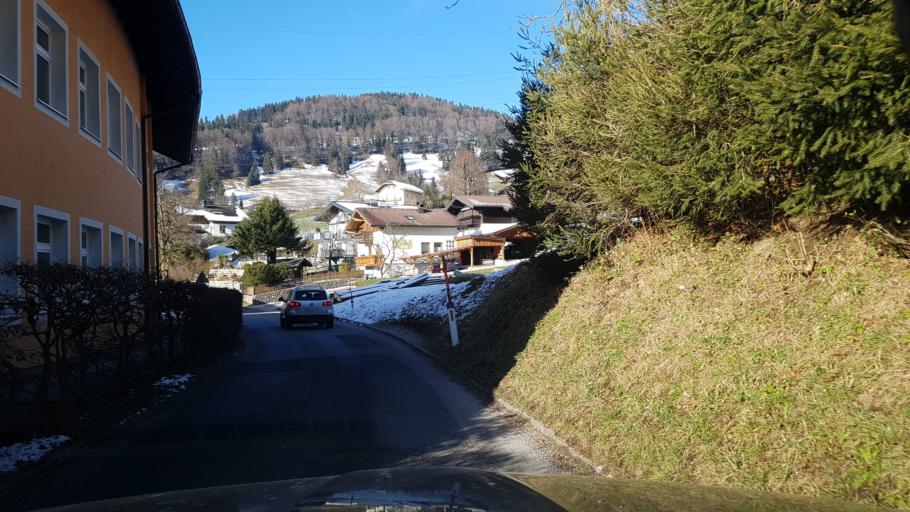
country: AT
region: Salzburg
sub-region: Politischer Bezirk Salzburg-Umgebung
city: Koppl
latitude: 47.7747
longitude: 13.1257
